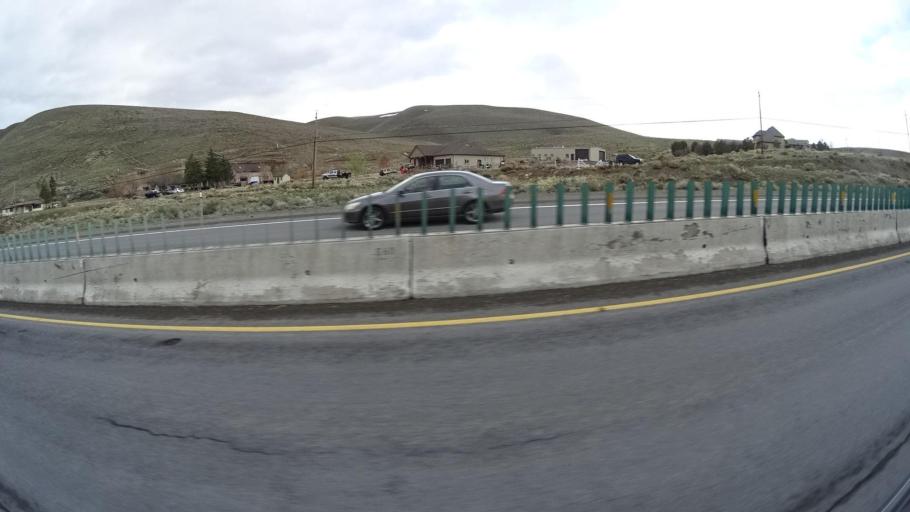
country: US
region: Nevada
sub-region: Storey County
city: Virginia City
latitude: 39.3351
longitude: -119.7815
